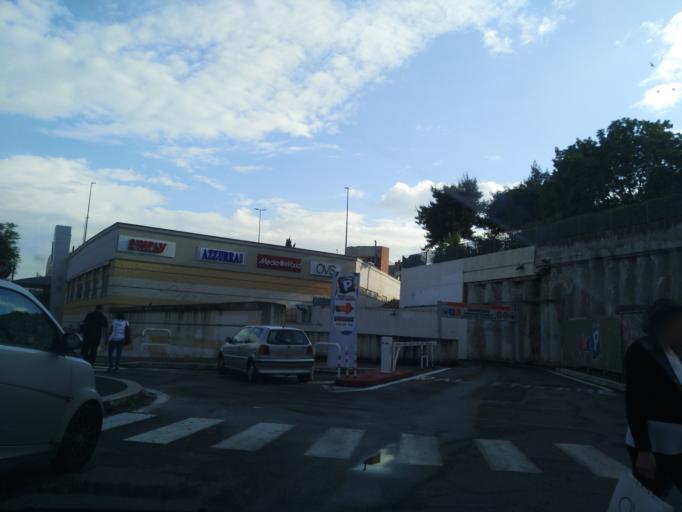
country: IT
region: Latium
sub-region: Citta metropolitana di Roma Capitale
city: Rome
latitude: 41.8829
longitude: 12.5606
